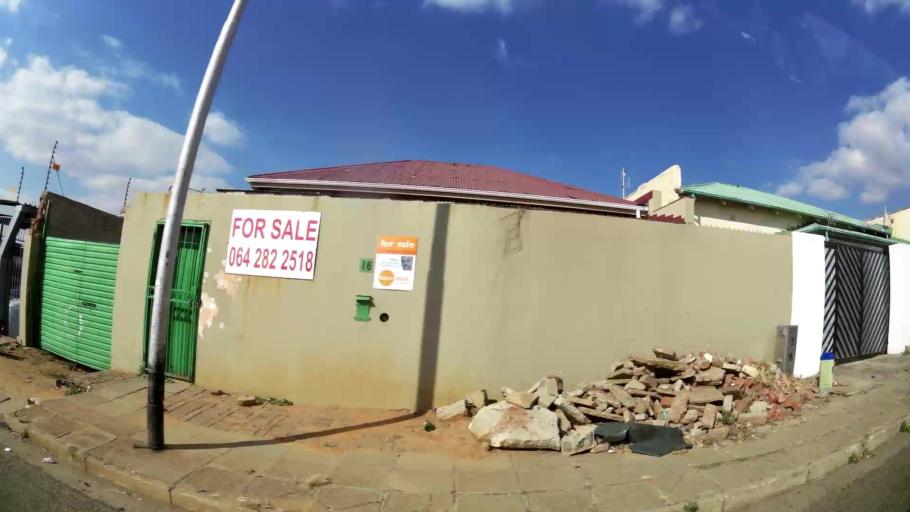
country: ZA
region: Gauteng
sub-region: West Rand District Municipality
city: Krugersdorp
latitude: -26.1070
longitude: 27.7753
